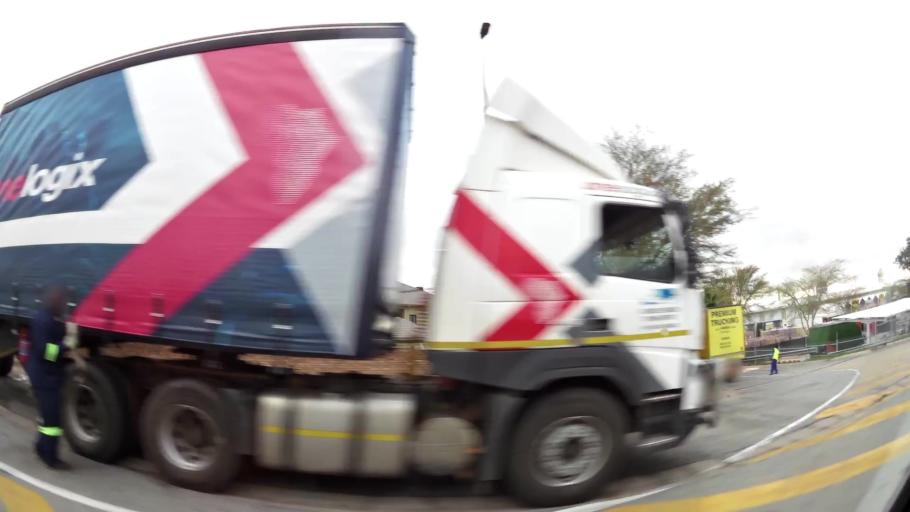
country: ZA
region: Limpopo
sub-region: Capricorn District Municipality
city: Polokwane
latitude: -23.9192
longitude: 29.4395
